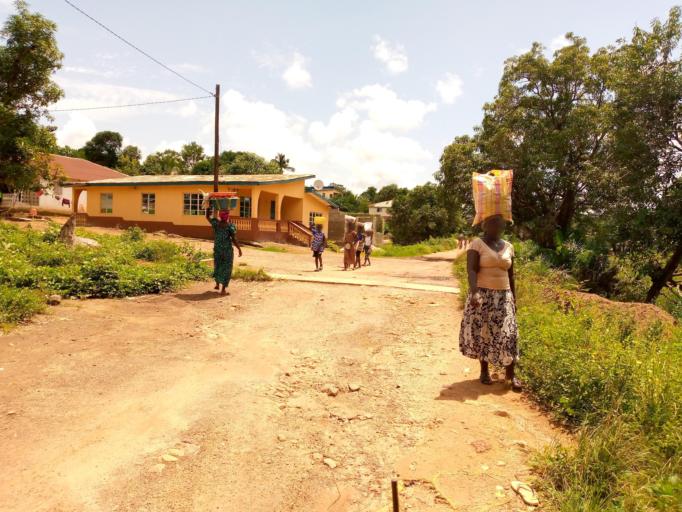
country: SL
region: Northern Province
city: Magburaka
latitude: 8.7265
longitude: -11.9423
